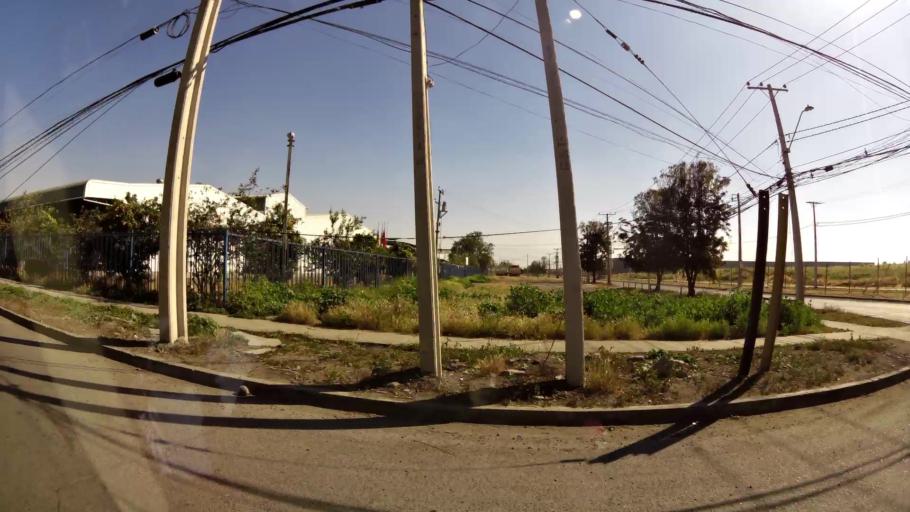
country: CL
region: Santiago Metropolitan
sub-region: Provincia de Chacabuco
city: Chicureo Abajo
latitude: -33.3279
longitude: -70.7077
